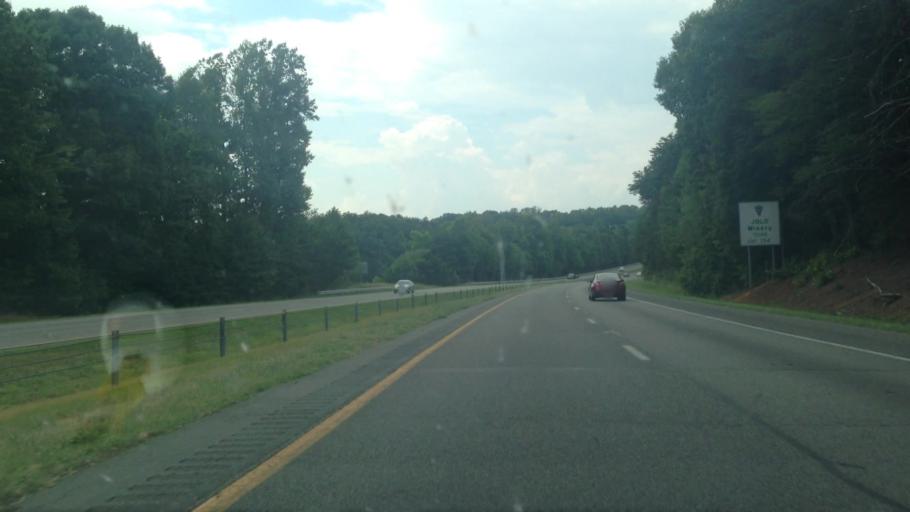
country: US
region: North Carolina
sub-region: Surry County
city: Pilot Mountain
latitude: 36.3591
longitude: -80.4766
